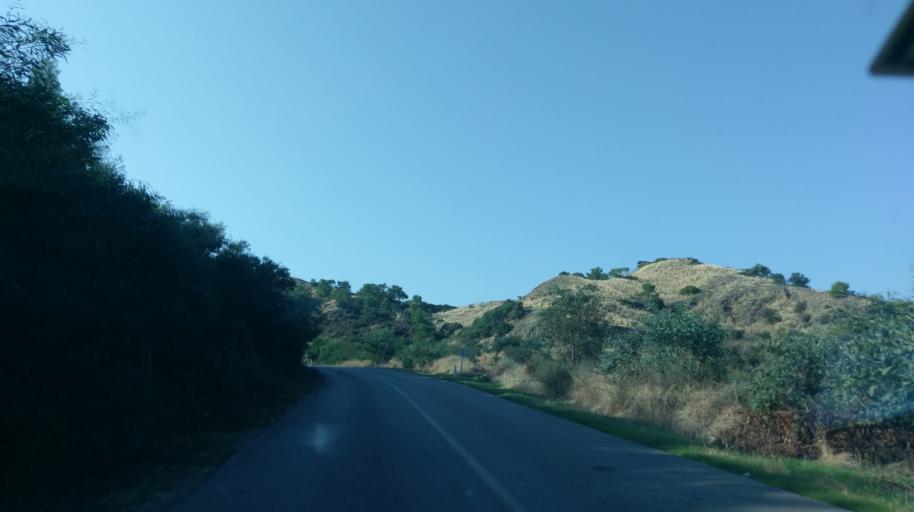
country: CY
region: Lefkosia
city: Kato Pyrgos
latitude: 35.1556
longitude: 32.7682
